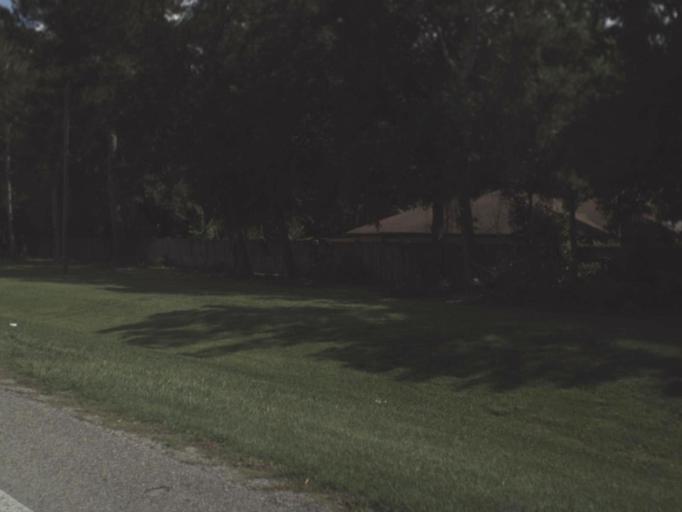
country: US
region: Florida
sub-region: Alachua County
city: Alachua
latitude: 29.7333
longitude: -82.3788
